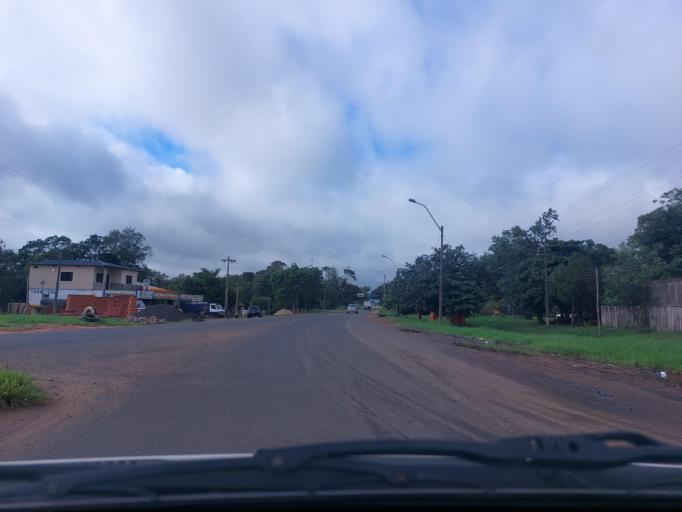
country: PY
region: San Pedro
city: Guayaybi
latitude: -24.5864
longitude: -56.4007
